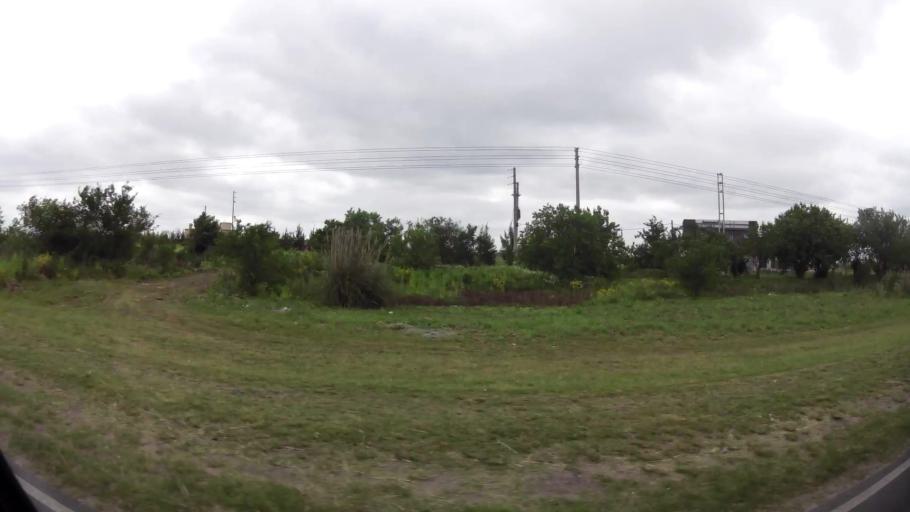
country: AR
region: Buenos Aires
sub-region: Partido de San Vicente
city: San Vicente
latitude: -34.9606
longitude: -58.4652
